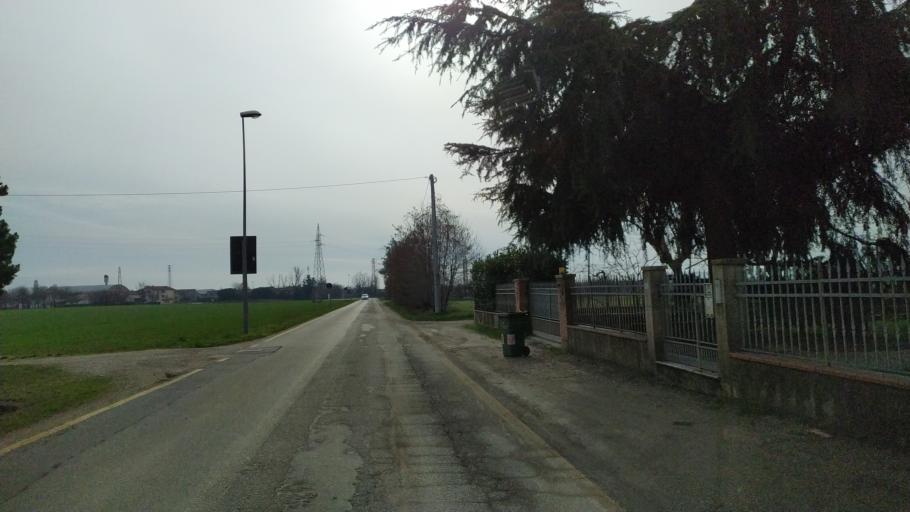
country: IT
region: Veneto
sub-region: Provincia di Vicenza
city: Villaverla
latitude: 45.6539
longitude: 11.4740
